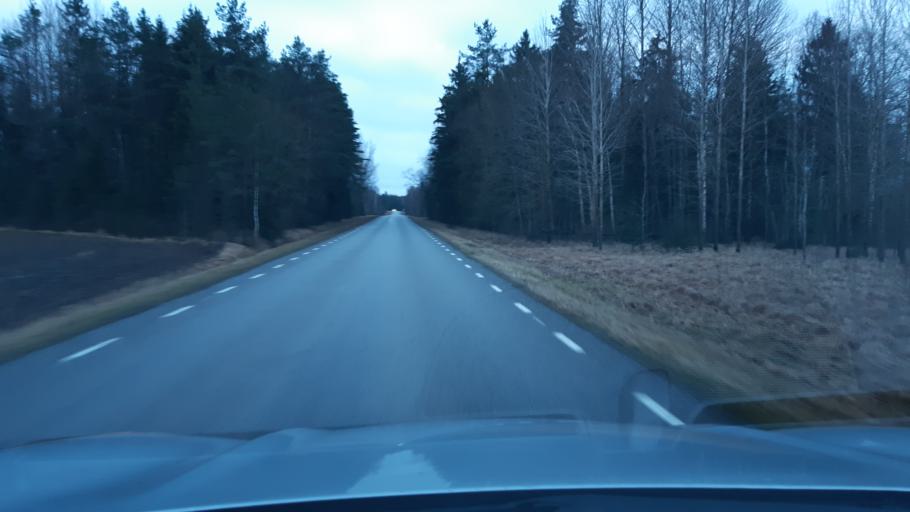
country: EE
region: Raplamaa
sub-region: Rapla vald
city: Rapla
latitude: 59.0311
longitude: 24.6785
